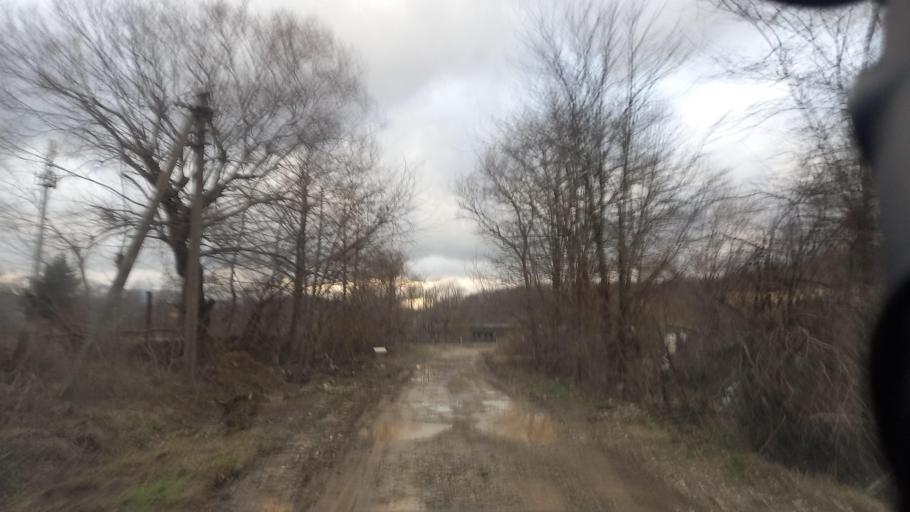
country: RU
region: Krasnodarskiy
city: Lermontovo
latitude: 44.4309
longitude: 38.7910
